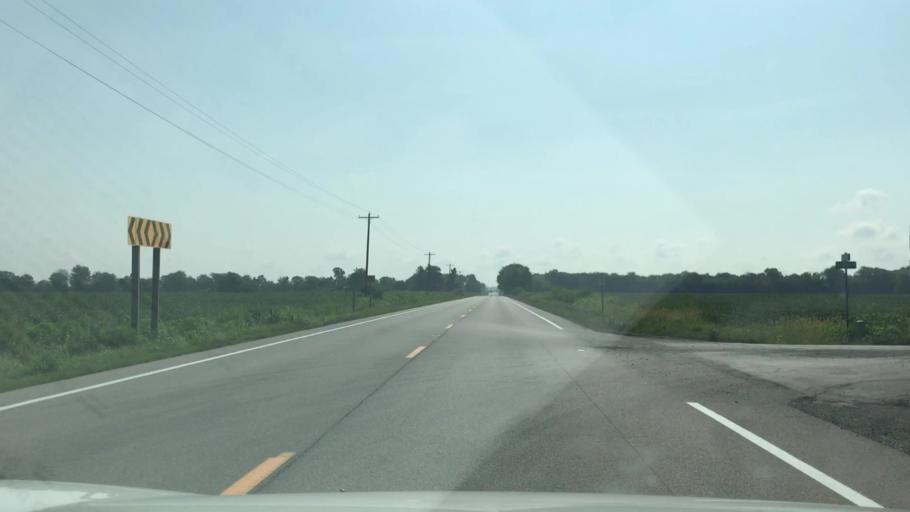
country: US
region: Illinois
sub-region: Washington County
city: Okawville
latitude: 38.4419
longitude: -89.4780
